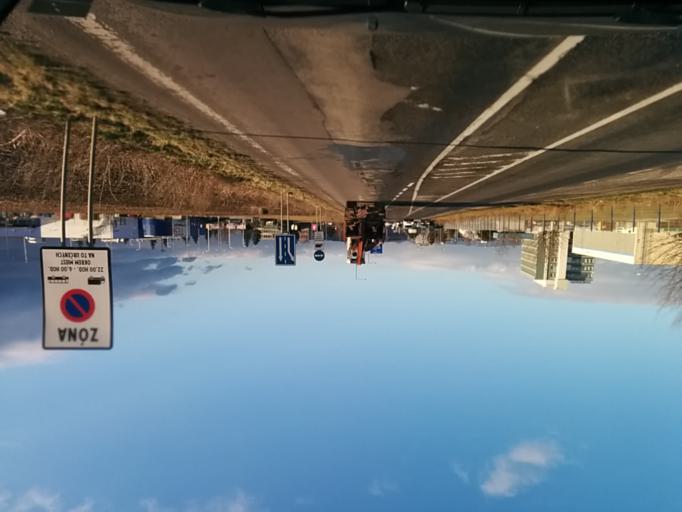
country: SK
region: Trenciansky
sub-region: Okres Nove Mesto nad Vahom
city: Nove Mesto nad Vahom
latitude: 48.7406
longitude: 17.8365
